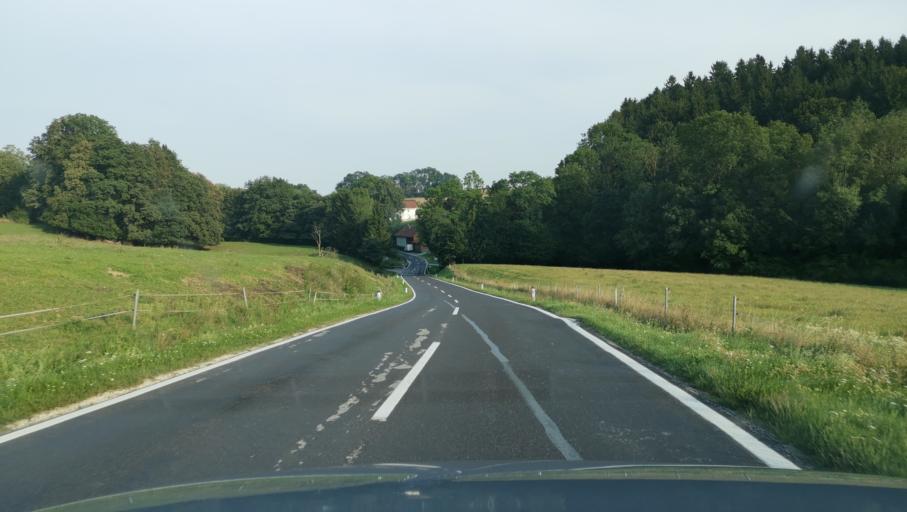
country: DE
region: Bavaria
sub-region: Lower Bavaria
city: Obernzell
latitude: 48.3658
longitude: 13.6671
